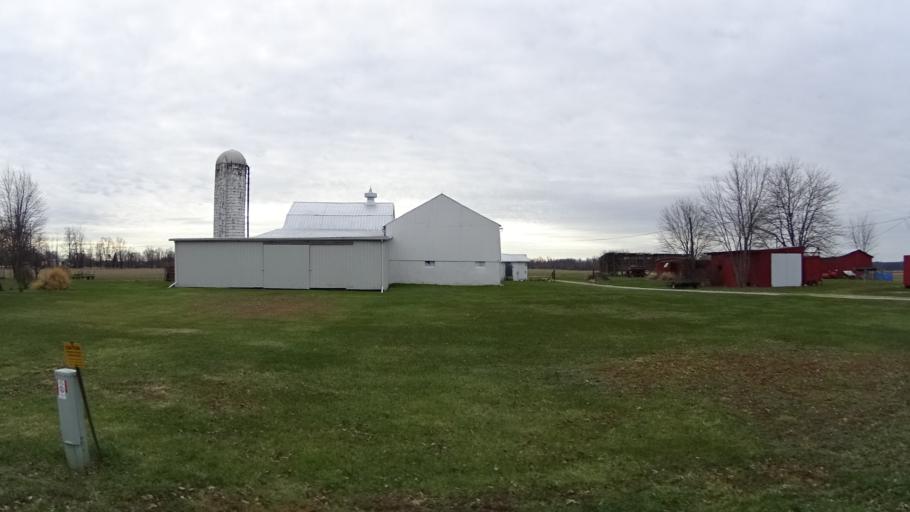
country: US
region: Ohio
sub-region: Lorain County
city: Wellington
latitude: 41.1474
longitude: -82.1753
